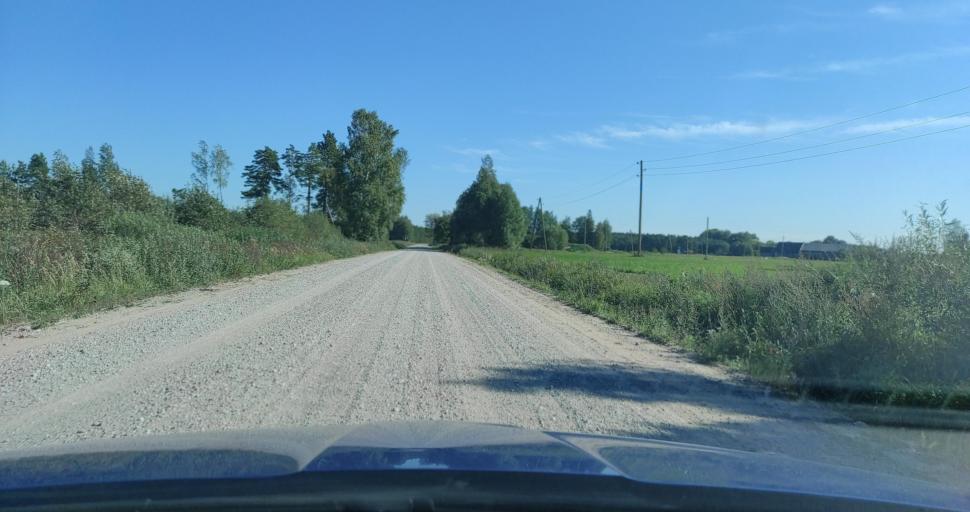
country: LV
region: Pavilostas
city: Pavilosta
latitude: 56.8511
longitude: 21.2723
